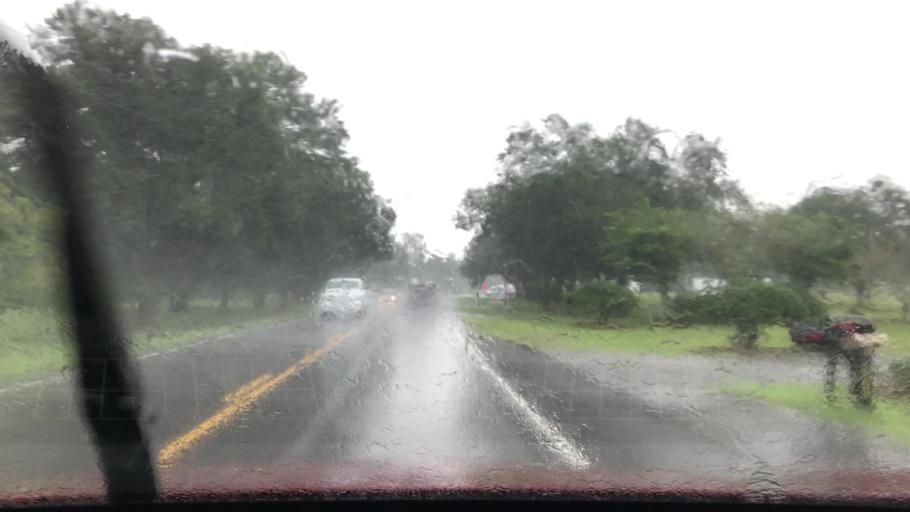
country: US
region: South Carolina
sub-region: Horry County
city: Loris
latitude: 33.9021
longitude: -78.8876
